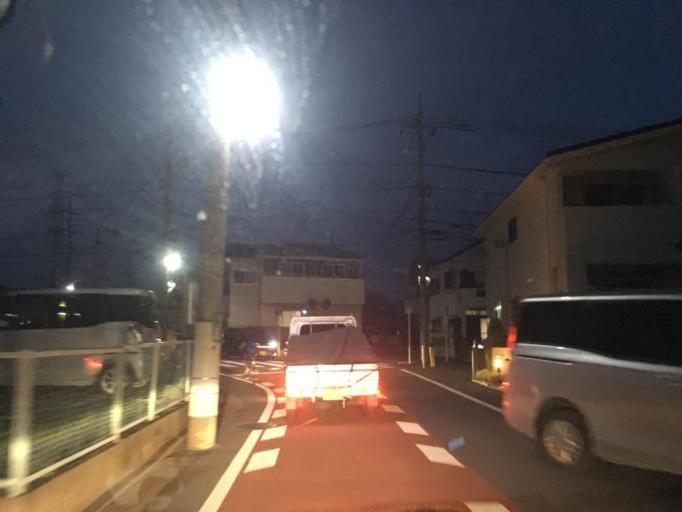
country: JP
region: Tokyo
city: Higashimurayama-shi
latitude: 35.7463
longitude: 139.4515
